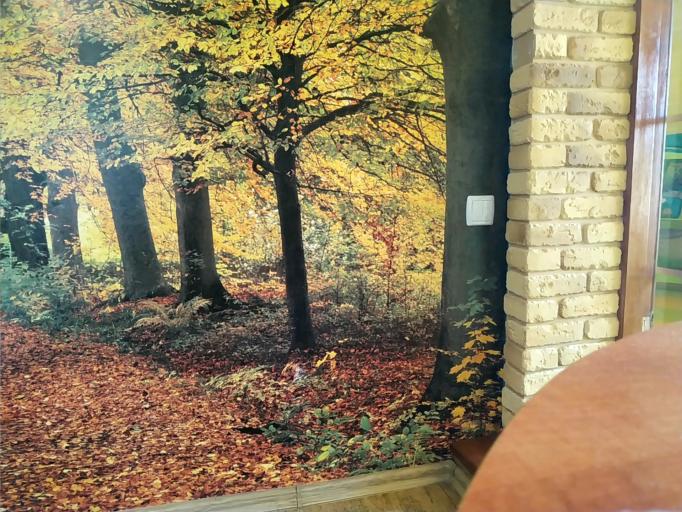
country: RU
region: Arkhangelskaya
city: Onega
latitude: 63.6623
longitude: 38.0984
